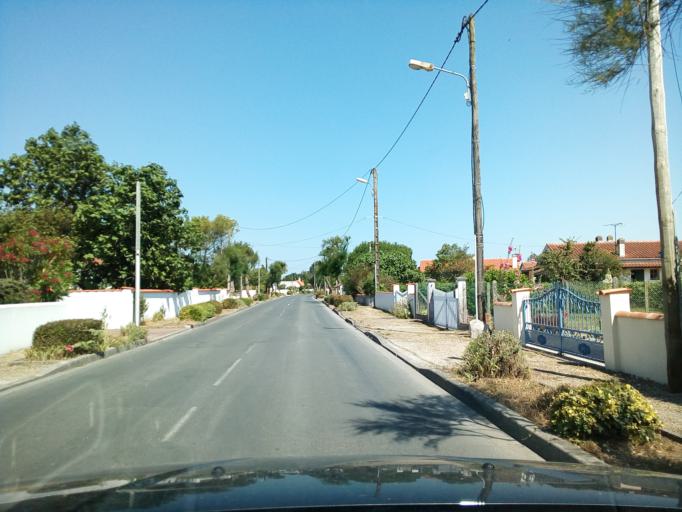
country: FR
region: Poitou-Charentes
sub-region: Departement de la Charente-Maritime
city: Boyard-Ville
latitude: 45.9710
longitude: -1.2926
